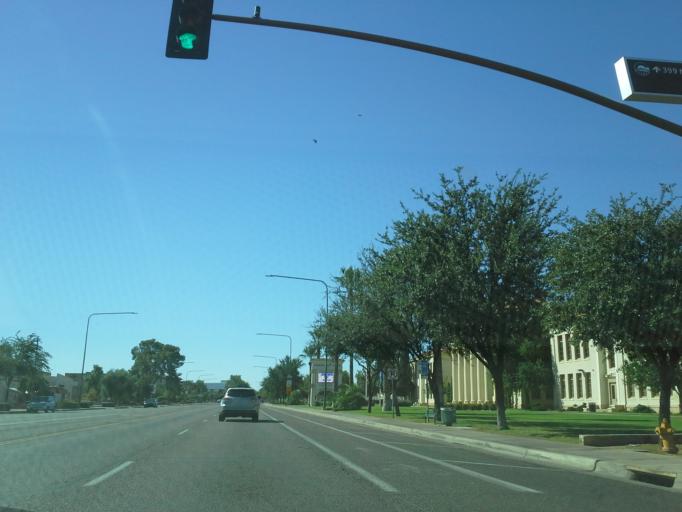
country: US
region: Arizona
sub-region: Maricopa County
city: Chandler
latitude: 33.3099
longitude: -111.8415
